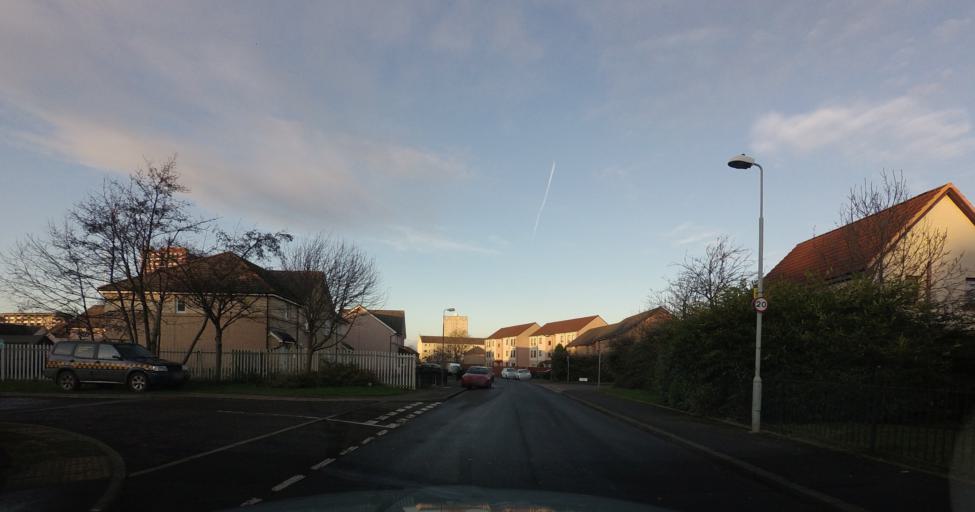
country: GB
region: Scotland
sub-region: Edinburgh
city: Colinton
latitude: 55.9702
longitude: -3.2604
